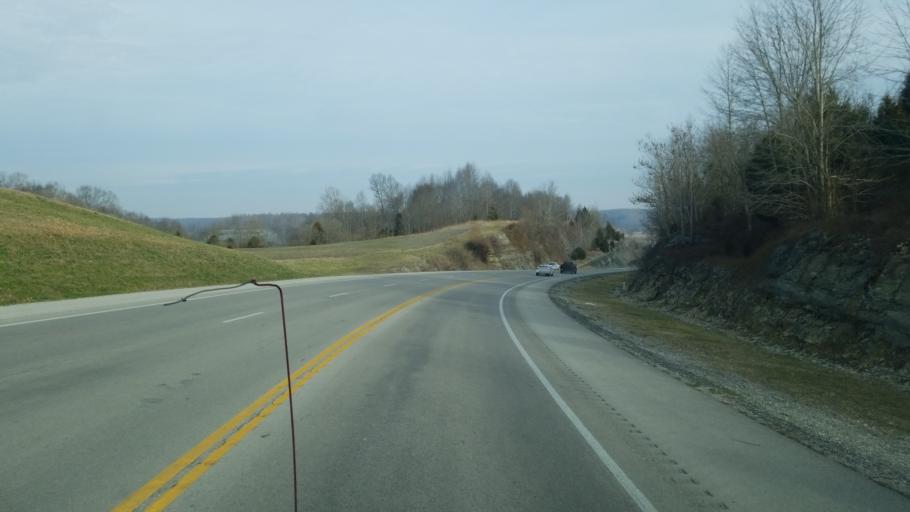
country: US
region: Kentucky
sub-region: Casey County
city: Liberty
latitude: 37.2845
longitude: -84.9589
